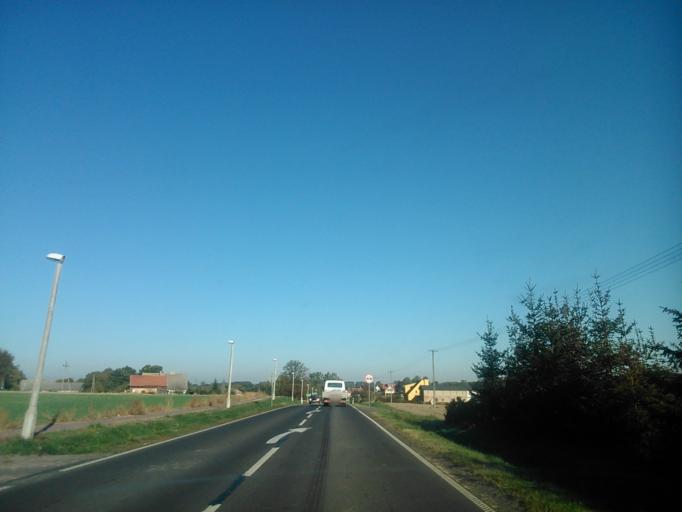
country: PL
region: Kujawsko-Pomorskie
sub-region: Powiat wabrzeski
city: Debowa Laka
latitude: 53.1969
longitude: 19.0383
